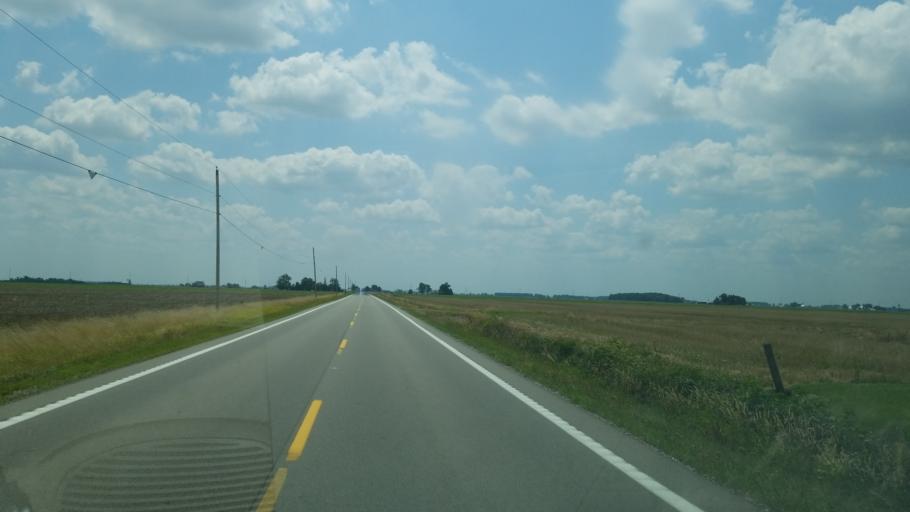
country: US
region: Ohio
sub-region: Henry County
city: Liberty Center
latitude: 41.3372
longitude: -83.9415
